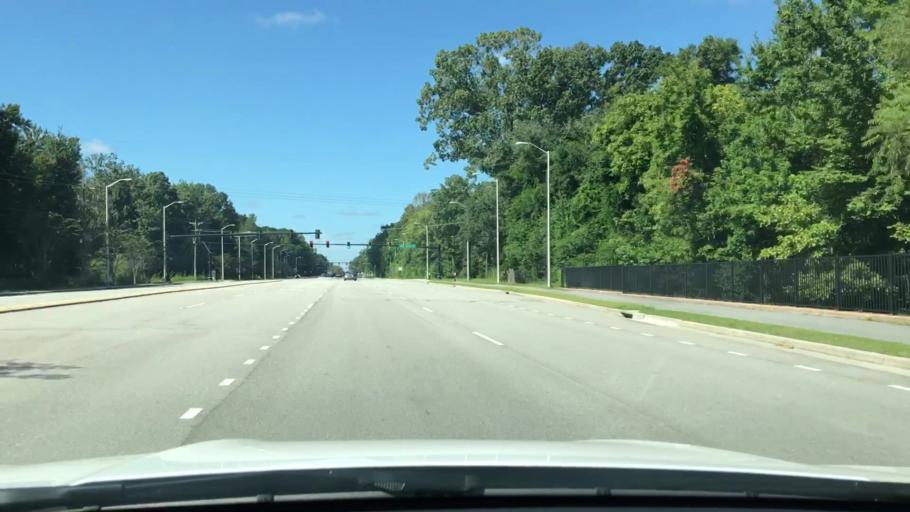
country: US
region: South Carolina
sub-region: Charleston County
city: Shell Point
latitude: 32.8276
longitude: -80.0756
